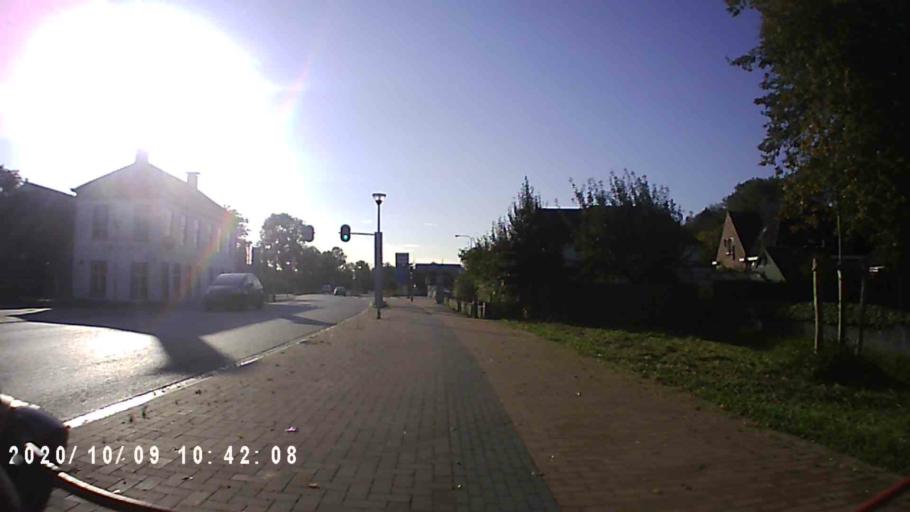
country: NL
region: Groningen
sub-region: Gemeente Groningen
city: Korrewegwijk
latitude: 53.2755
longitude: 6.5351
